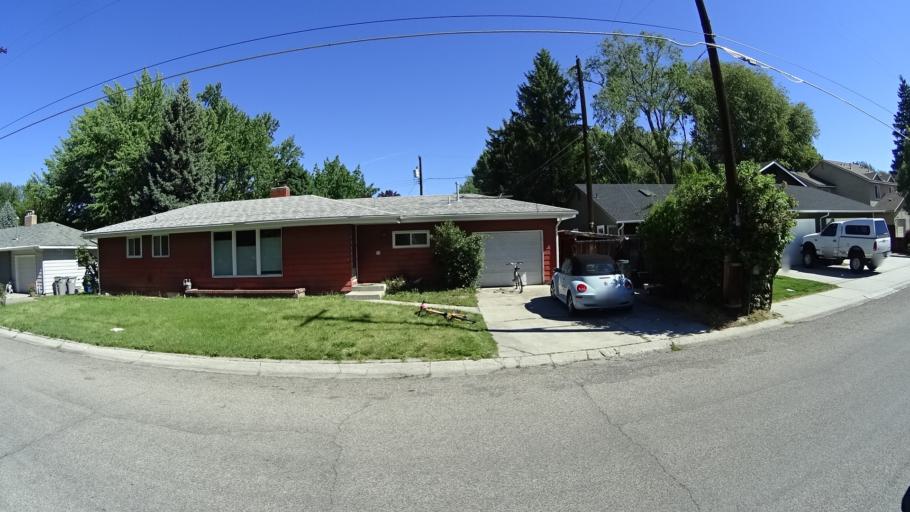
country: US
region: Idaho
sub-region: Ada County
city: Garden City
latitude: 43.6481
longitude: -116.2347
